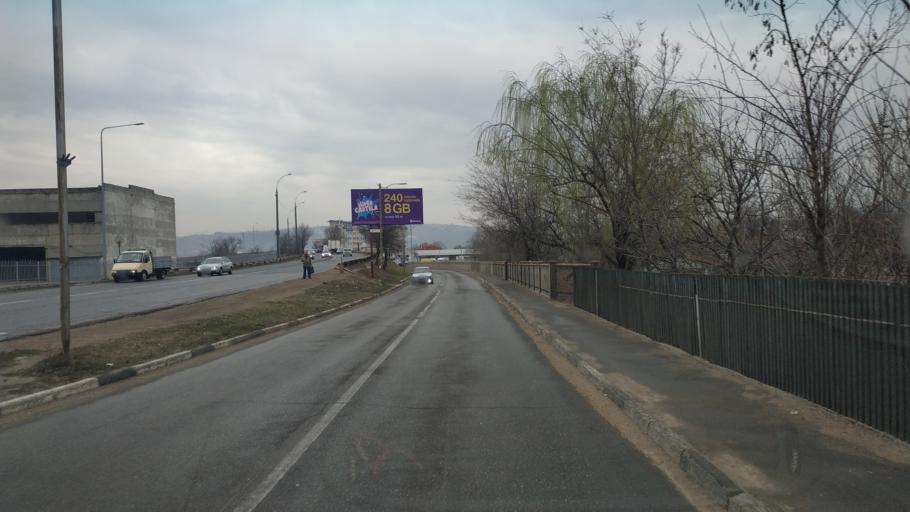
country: MD
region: Chisinau
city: Singera
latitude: 46.9215
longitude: 28.9700
